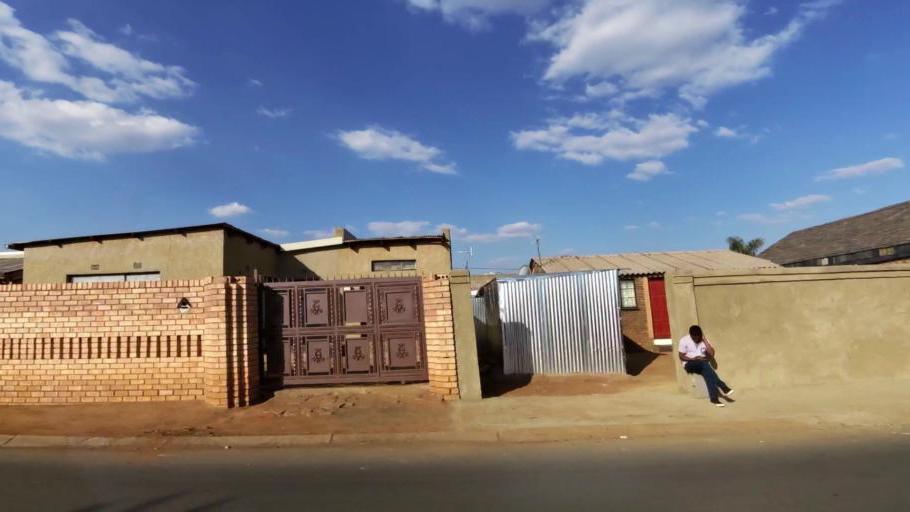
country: ZA
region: Gauteng
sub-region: City of Johannesburg Metropolitan Municipality
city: Roodepoort
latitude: -26.2083
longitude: 27.8776
